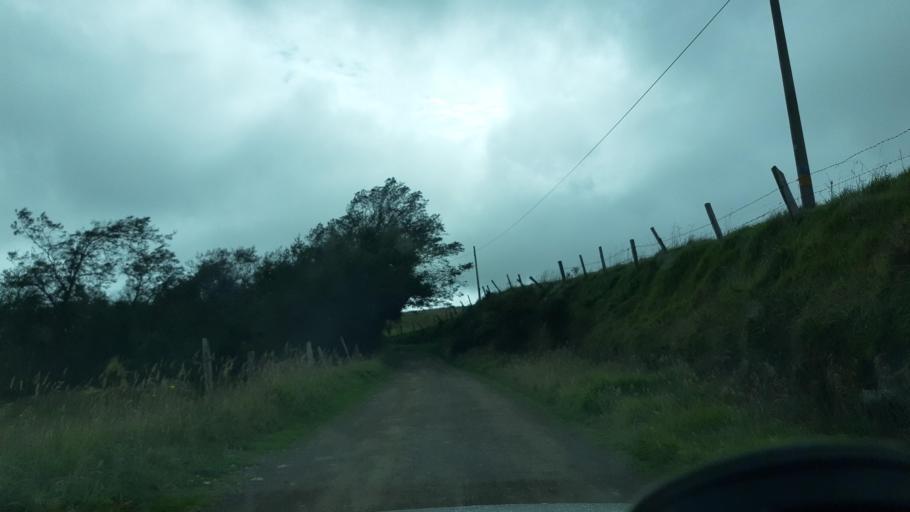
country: CO
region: Boyaca
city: Cucaita
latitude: 5.5069
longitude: -73.4364
